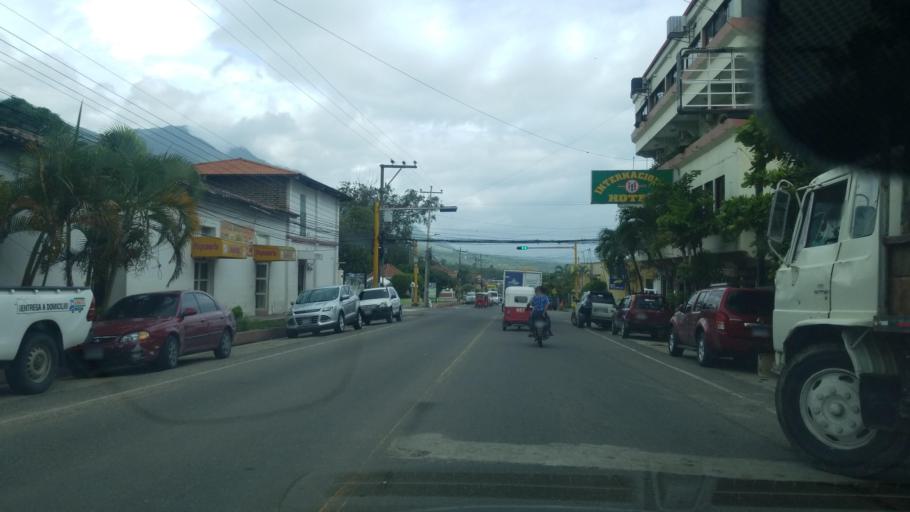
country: HN
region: Ocotepeque
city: Nueva Ocotepeque
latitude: 14.4356
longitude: -89.1828
